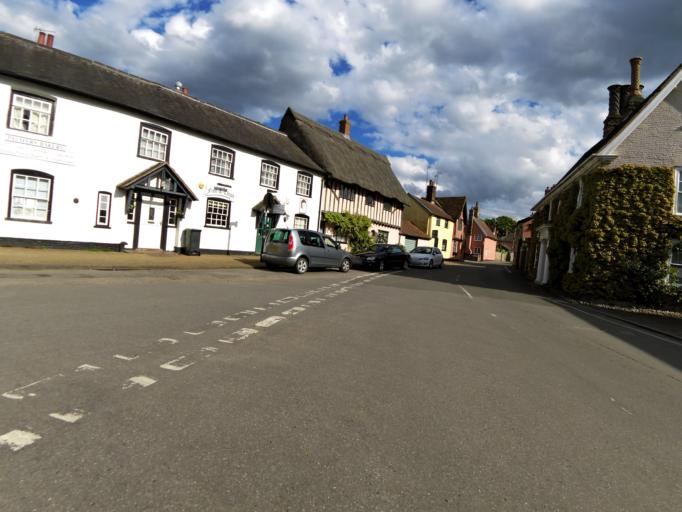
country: GB
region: England
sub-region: Suffolk
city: Woolpit
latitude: 52.2243
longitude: 0.8885
